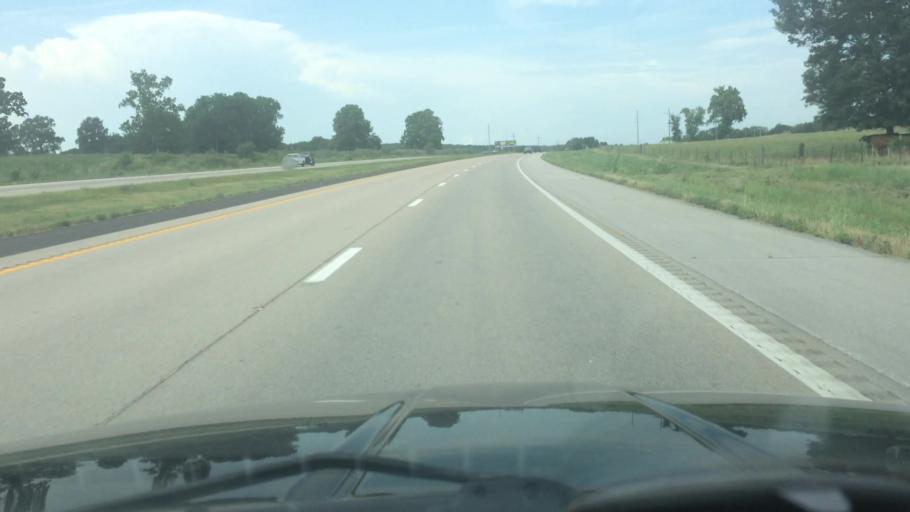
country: US
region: Missouri
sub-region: Polk County
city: Humansville
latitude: 37.8241
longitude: -93.6165
